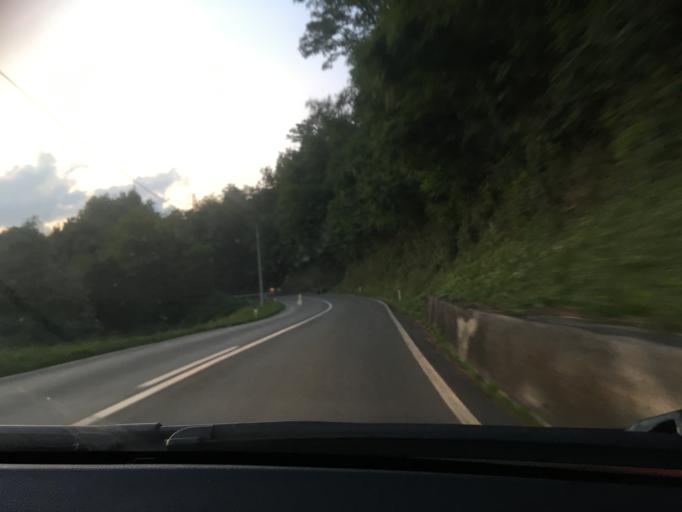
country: SI
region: Pivka
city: Pivka
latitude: 45.6170
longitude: 14.1762
